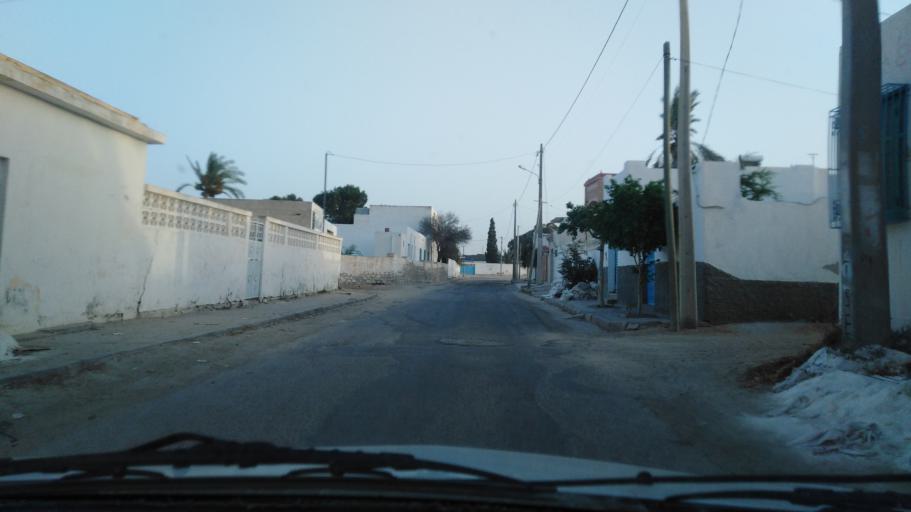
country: TN
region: Qabis
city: Gabes
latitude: 33.9585
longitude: 10.0019
